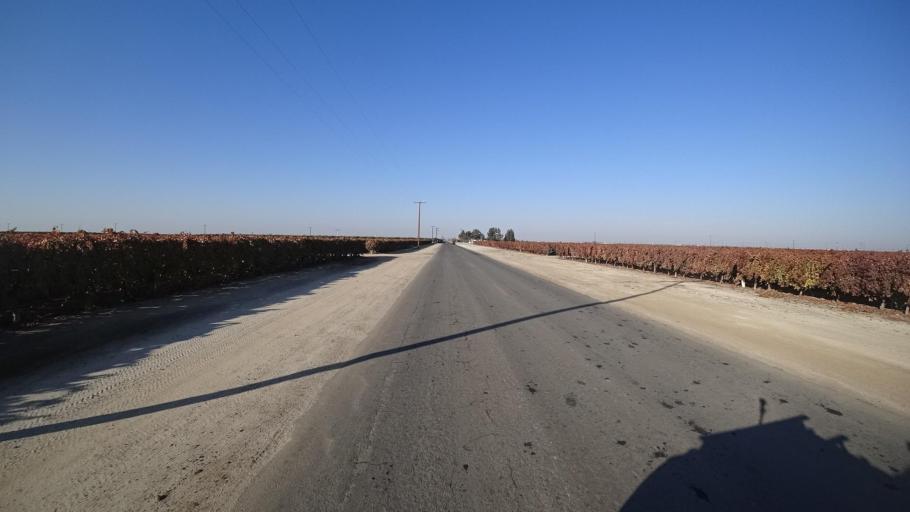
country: US
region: California
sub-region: Kern County
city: Delano
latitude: 35.7687
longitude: -119.1848
